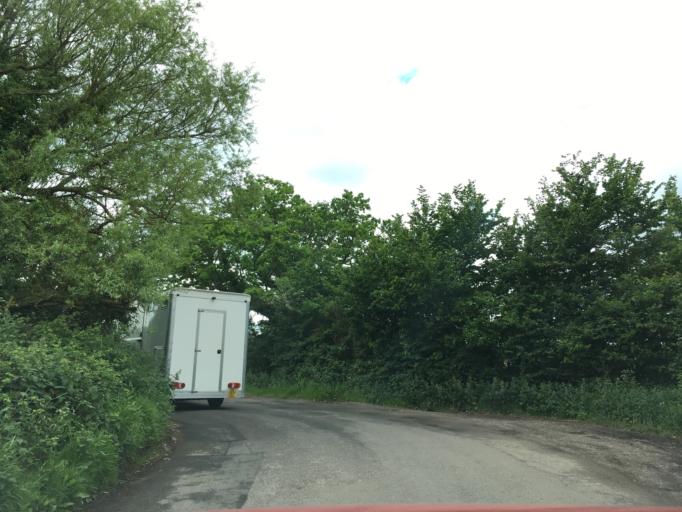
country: GB
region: England
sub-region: Somerset
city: Bishops Lydeard
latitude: 50.9701
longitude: -3.1967
